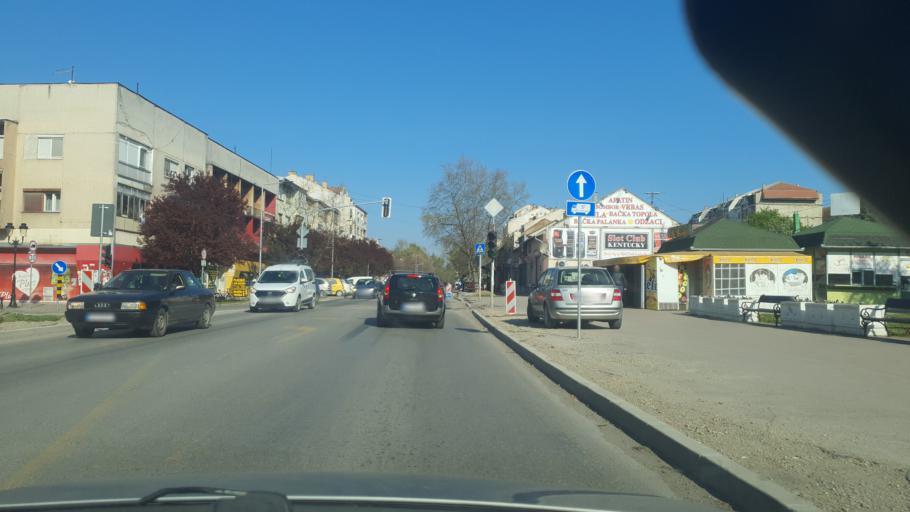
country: RS
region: Autonomna Pokrajina Vojvodina
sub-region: Zapadnobacki Okrug
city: Kula
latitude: 45.6094
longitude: 19.5330
